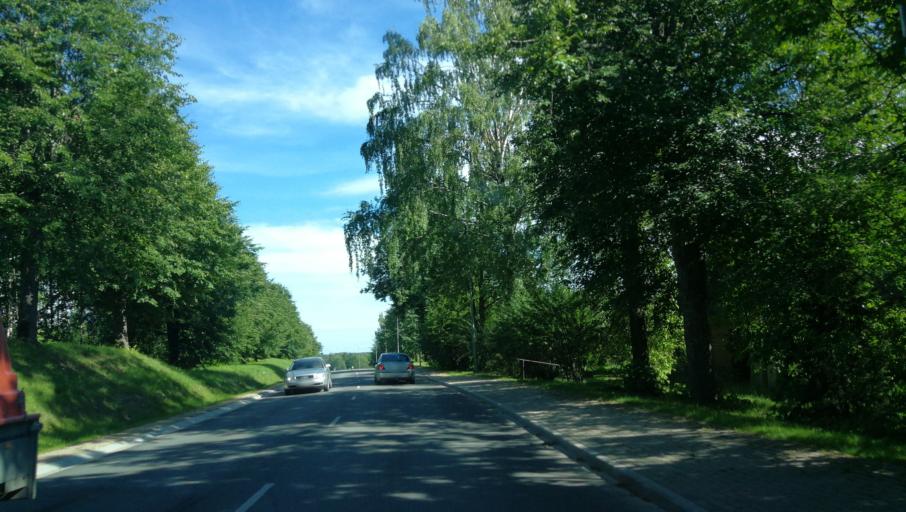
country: LV
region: Cesvaine
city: Cesvaine
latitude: 56.9661
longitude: 26.3190
